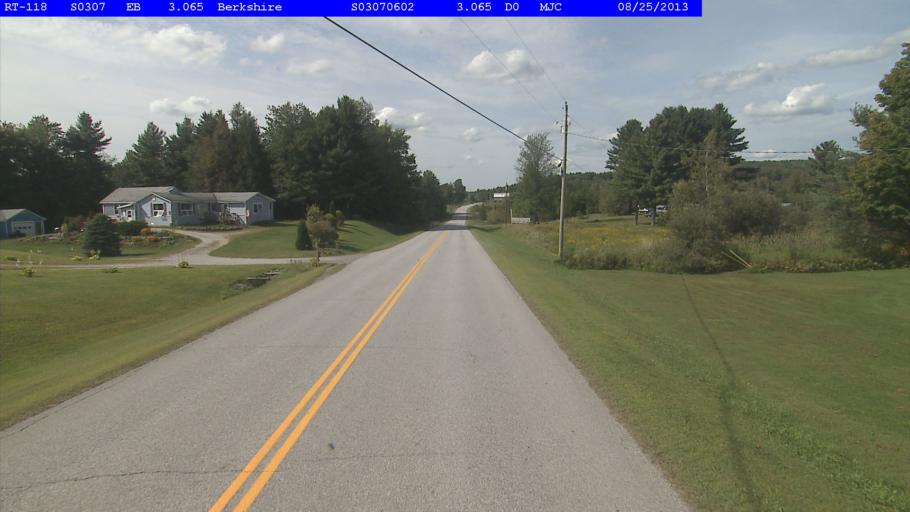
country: US
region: Vermont
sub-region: Franklin County
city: Enosburg Falls
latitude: 44.9598
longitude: -72.7569
